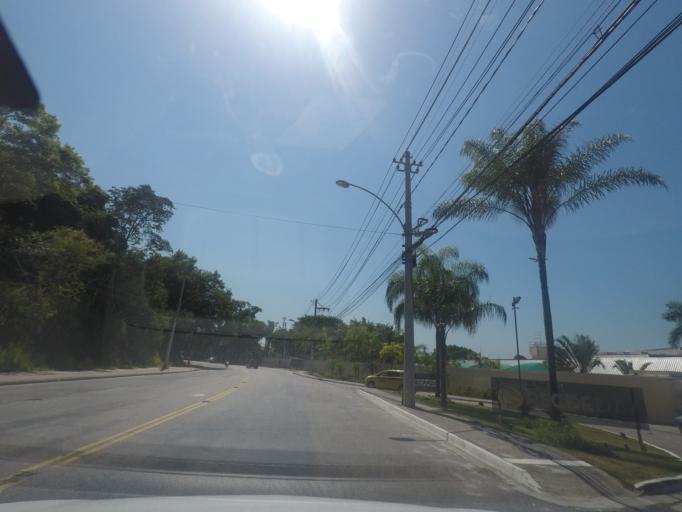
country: BR
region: Rio de Janeiro
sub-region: Nilopolis
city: Nilopolis
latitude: -22.9879
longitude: -43.4829
